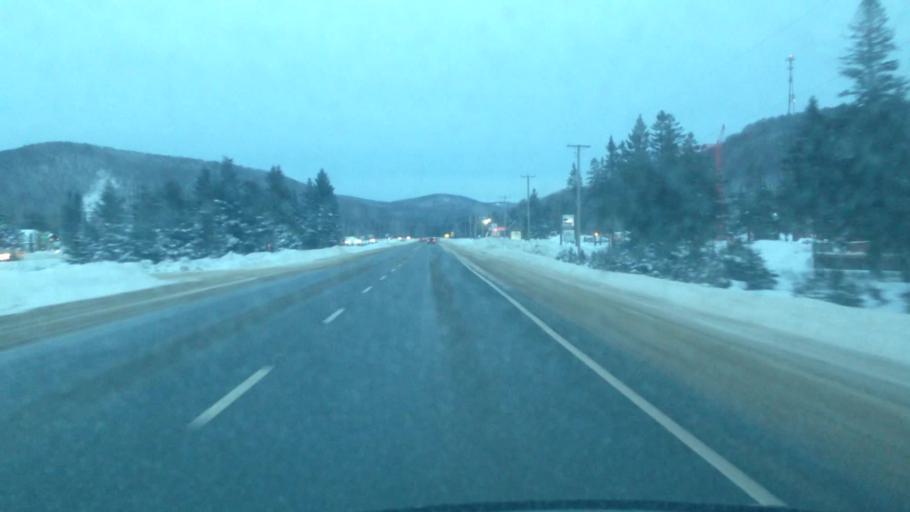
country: CA
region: Quebec
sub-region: Laurentides
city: Mont-Tremblant
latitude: 46.1216
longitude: -74.4582
